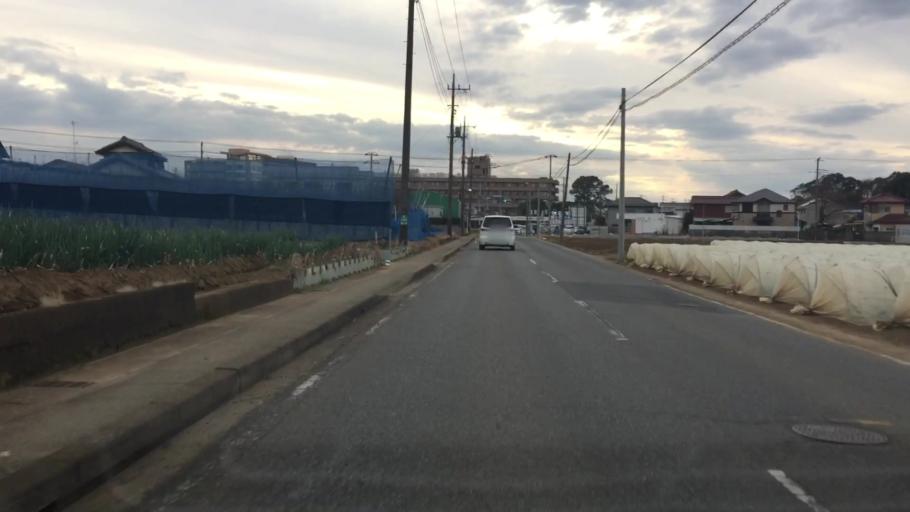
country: JP
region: Chiba
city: Kashiwa
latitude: 35.7875
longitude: 139.9890
